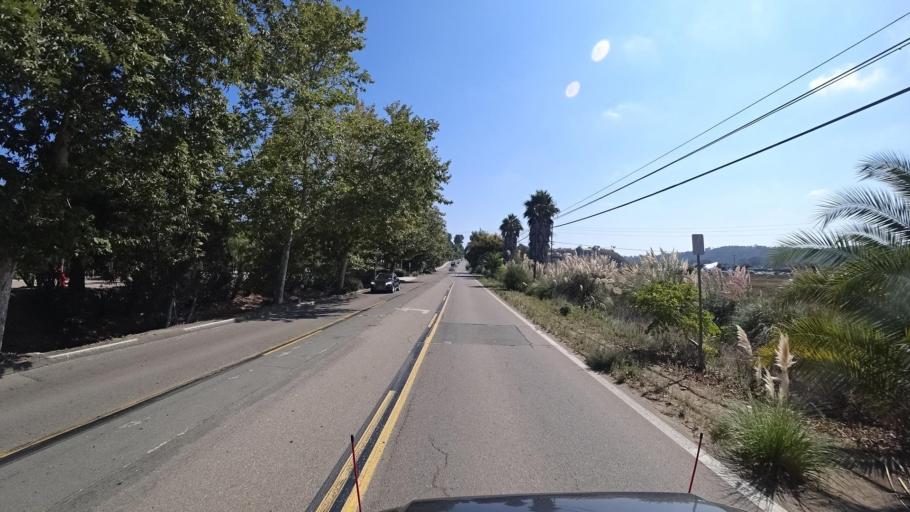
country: US
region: California
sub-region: San Diego County
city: Fairbanks Ranch
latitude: 32.9830
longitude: -117.2284
